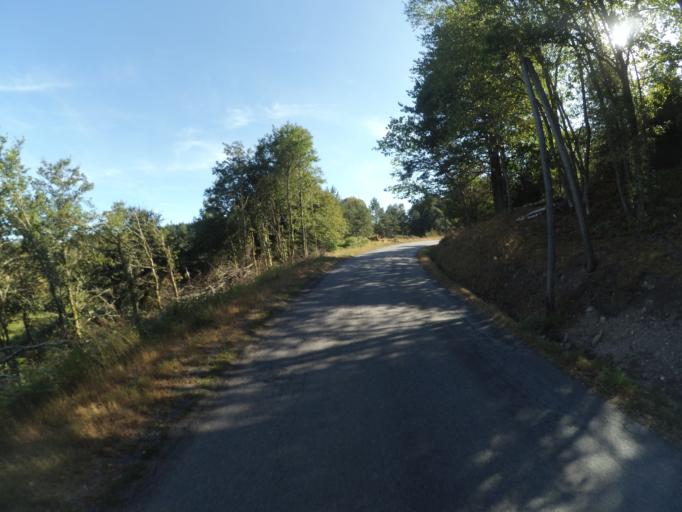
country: FR
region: Limousin
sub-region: Departement de la Correze
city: Bugeat
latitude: 45.6959
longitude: 1.9964
